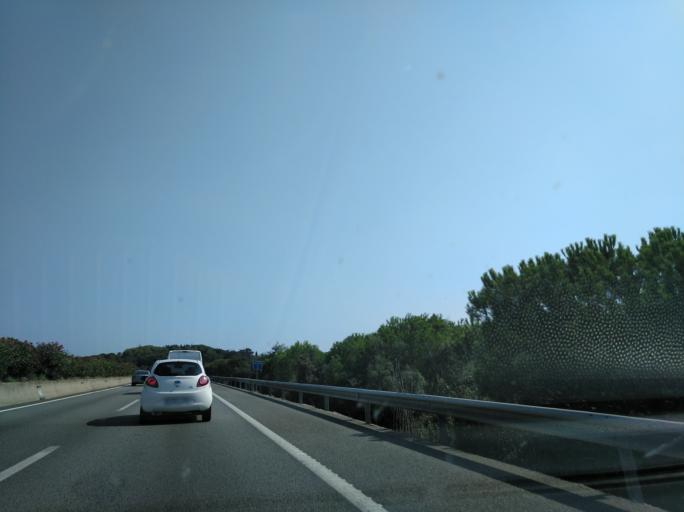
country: ES
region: Catalonia
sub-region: Provincia de Barcelona
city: Argentona
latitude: 41.5649
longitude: 2.3978
